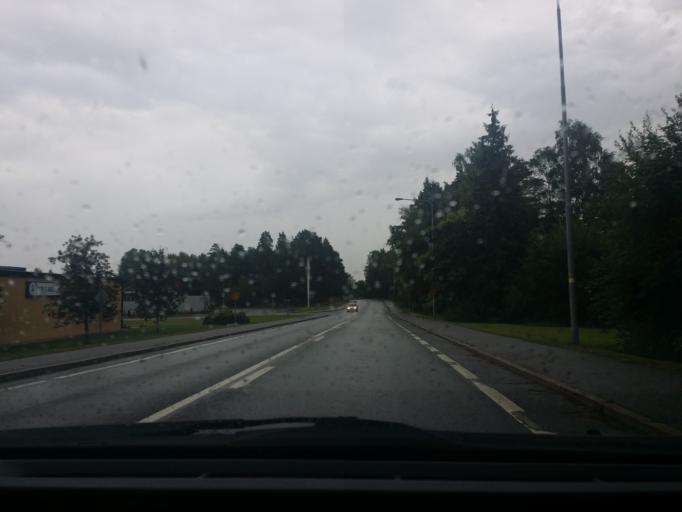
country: SE
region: OErebro
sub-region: Lindesbergs Kommun
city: Frovi
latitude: 59.4683
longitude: 15.3519
